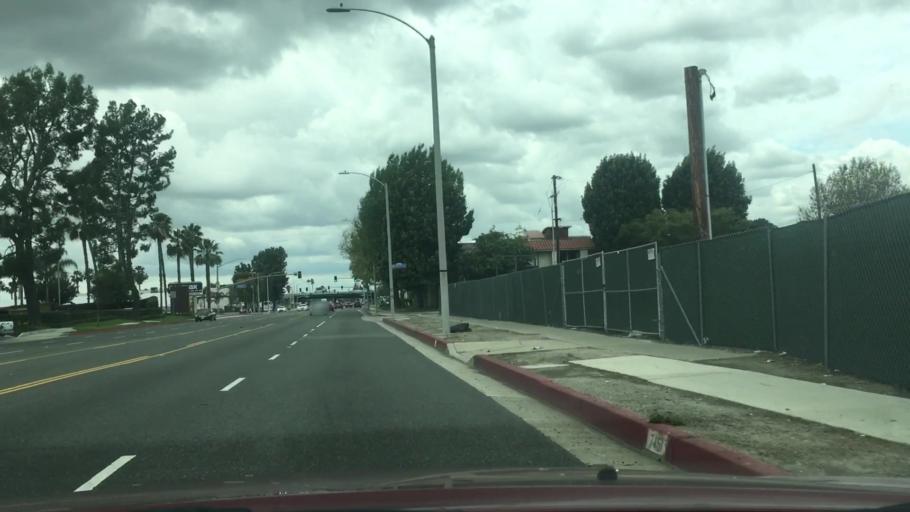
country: US
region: California
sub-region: Orange County
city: Buena Park
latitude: 33.8736
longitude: -118.0033
